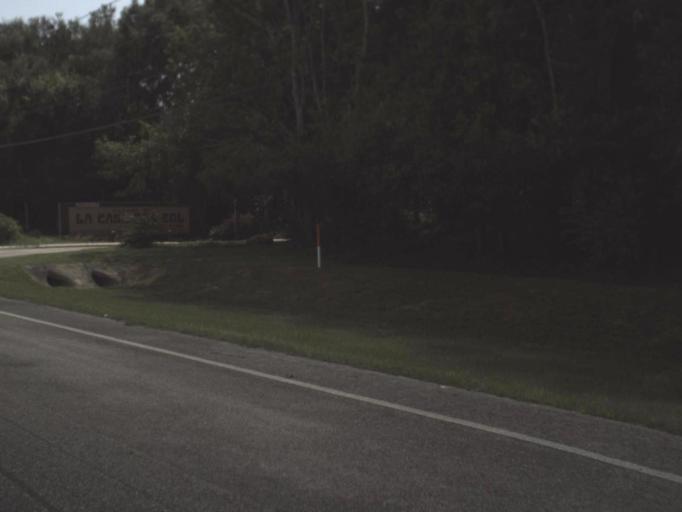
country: US
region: Florida
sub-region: Polk County
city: Davenport
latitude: 28.1744
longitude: -81.6400
